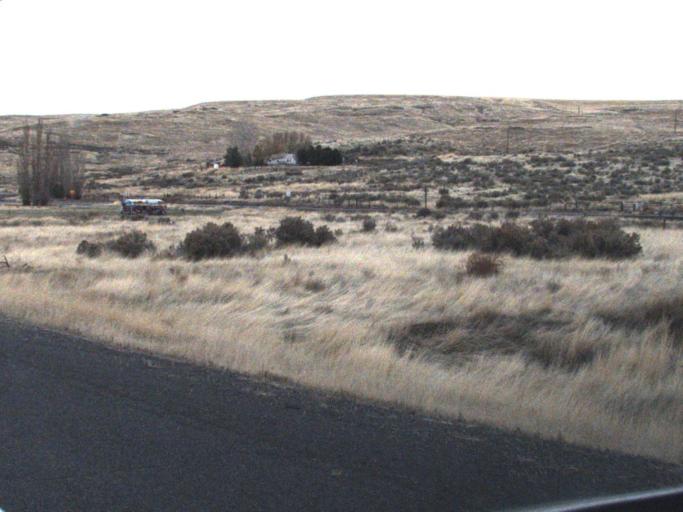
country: US
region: Washington
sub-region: Adams County
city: Ritzville
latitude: 46.7579
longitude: -118.3035
